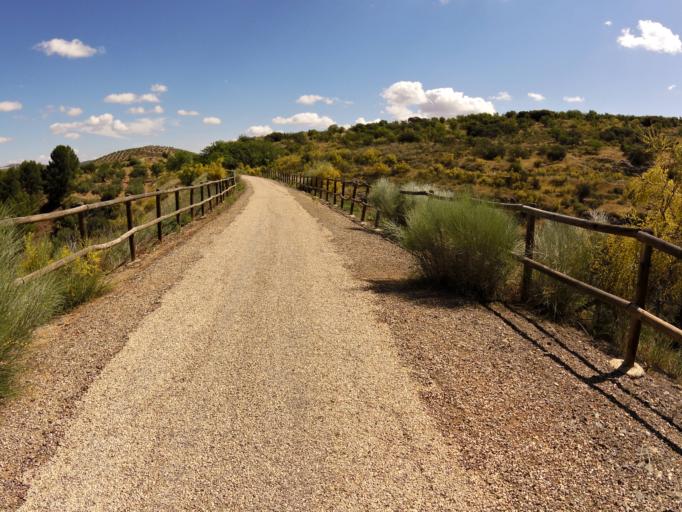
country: ES
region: Andalusia
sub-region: Provincia de Jaen
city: Alcaudete
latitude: 37.6157
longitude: -4.1103
